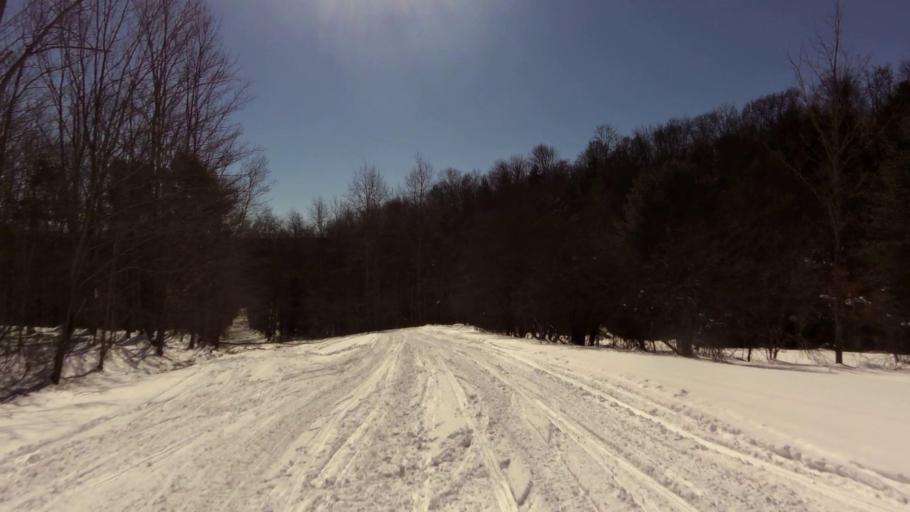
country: US
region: New York
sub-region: Allegany County
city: Cuba
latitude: 42.2831
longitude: -78.2336
